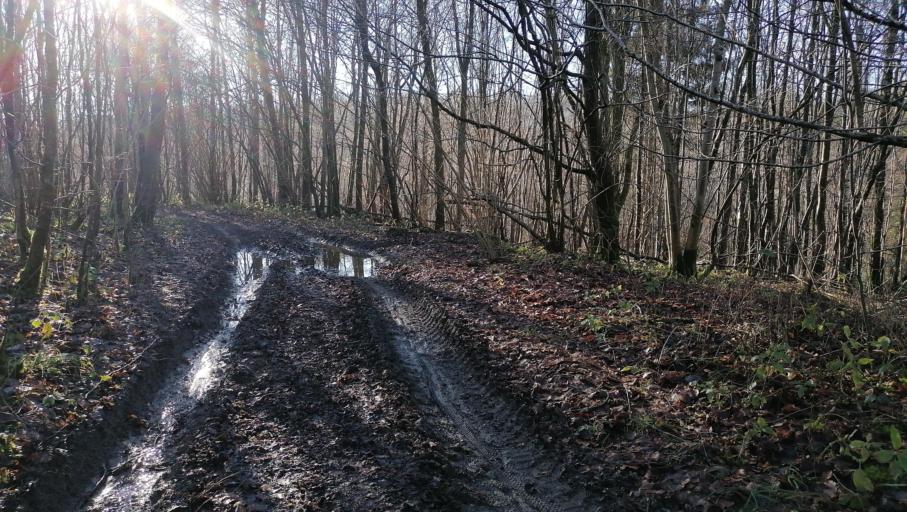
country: FR
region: Nord-Pas-de-Calais
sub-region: Departement du Nord
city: Recquignies
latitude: 50.1968
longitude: 4.0663
